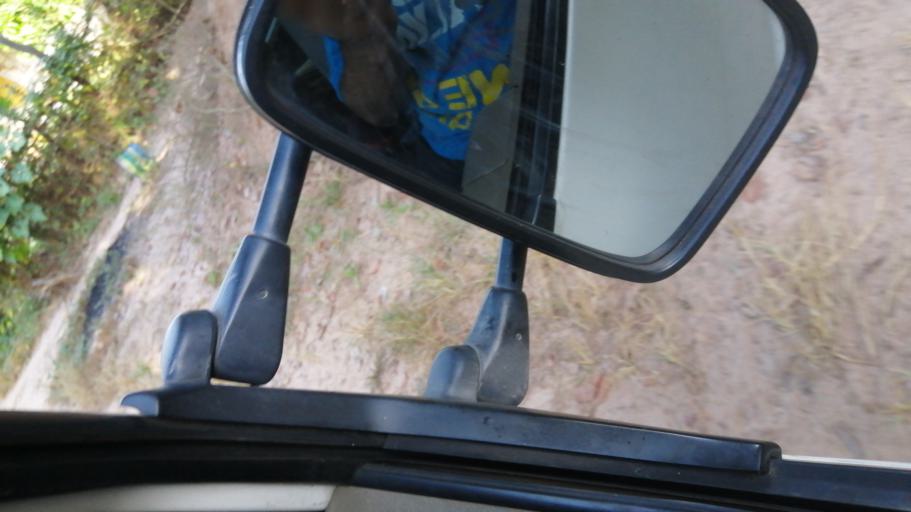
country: GW
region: Oio
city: Mansoa
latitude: 11.9994
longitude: -15.4694
